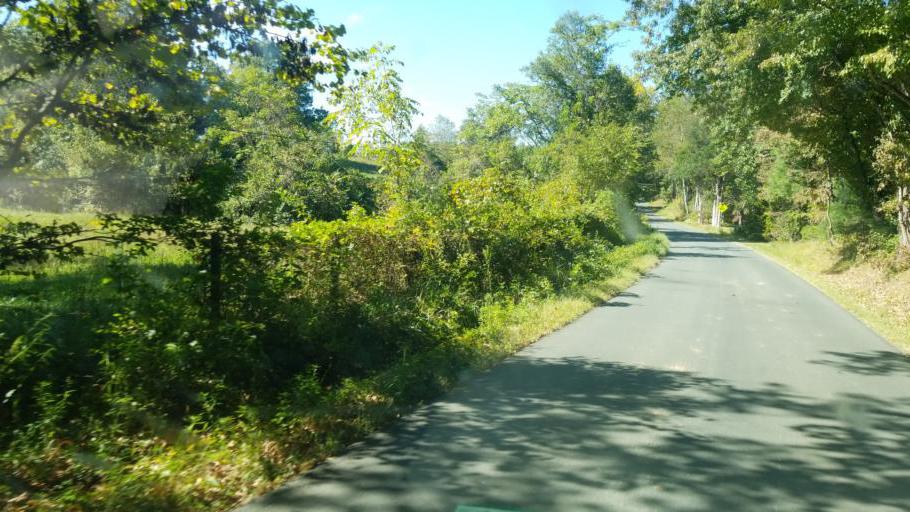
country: US
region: Virginia
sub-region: Greene County
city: Stanardsville
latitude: 38.3515
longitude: -78.3898
